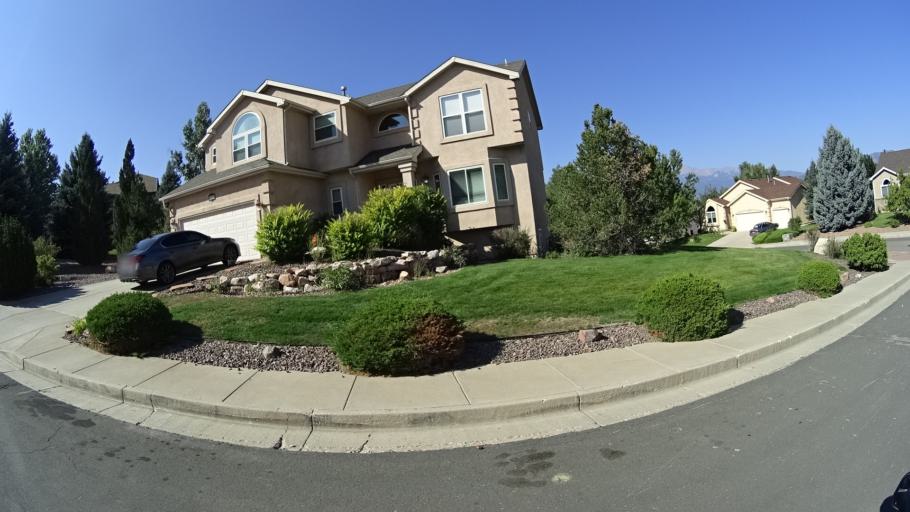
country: US
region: Colorado
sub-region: El Paso County
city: Colorado Springs
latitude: 38.8845
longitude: -104.7854
